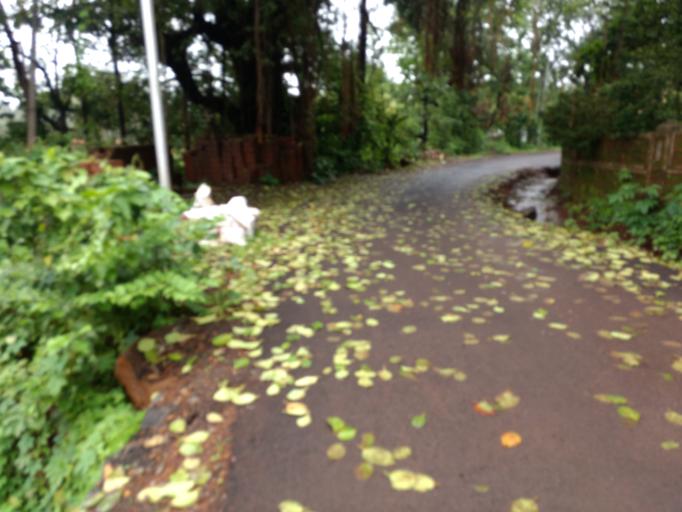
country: IN
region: Maharashtra
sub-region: Ratnagiri
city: Guhagar
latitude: 17.4942
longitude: 73.1893
